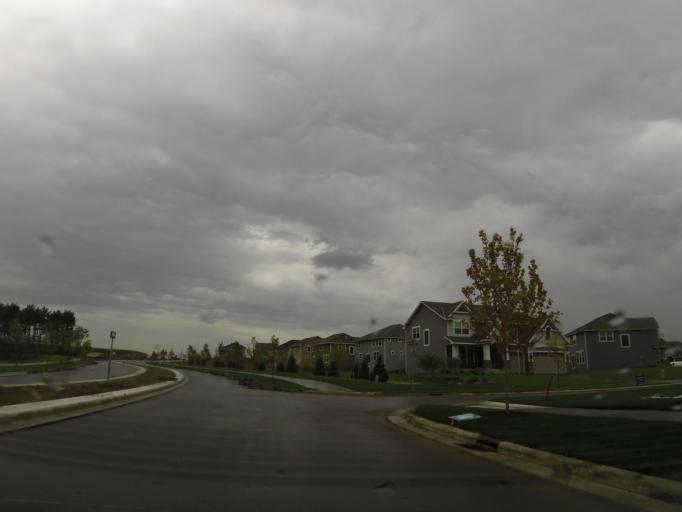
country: US
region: Minnesota
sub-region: Washington County
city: Lake Elmo
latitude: 44.9551
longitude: -92.9053
